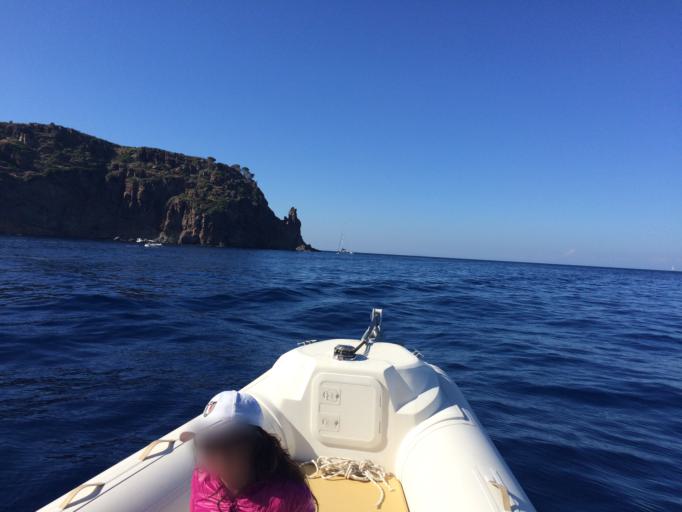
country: IT
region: Tuscany
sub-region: Provincia di Livorno
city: Capraia Isola
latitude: 43.0404
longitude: 9.8487
